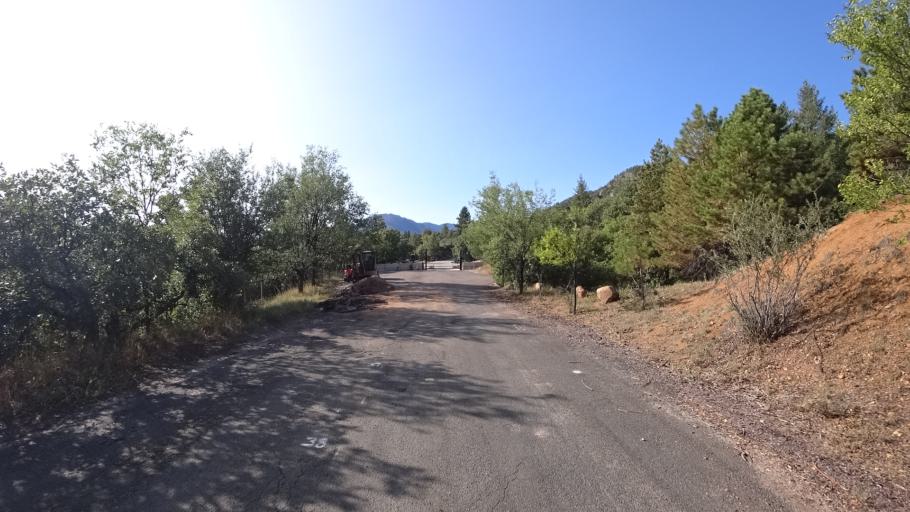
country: US
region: Colorado
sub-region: El Paso County
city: Colorado Springs
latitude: 38.8079
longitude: -104.8733
